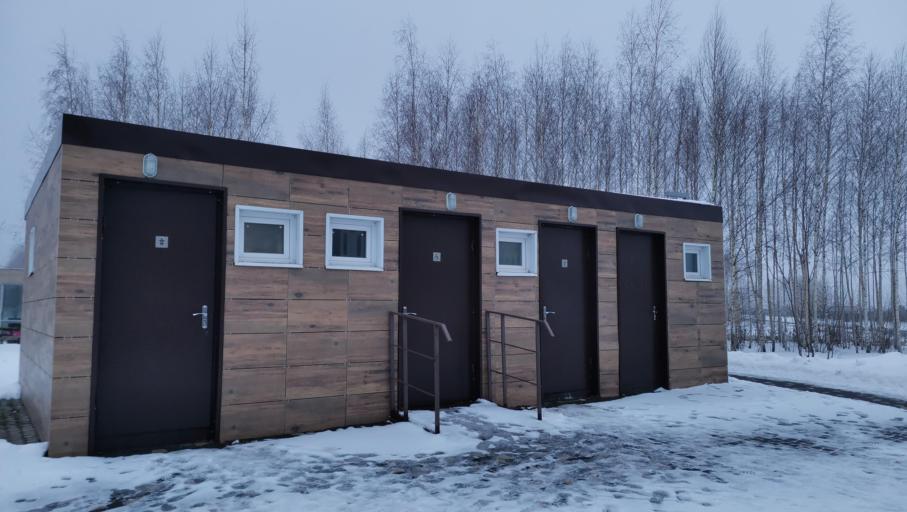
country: RU
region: Tatarstan
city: Sviyazhsk
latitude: 55.7462
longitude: 48.7437
